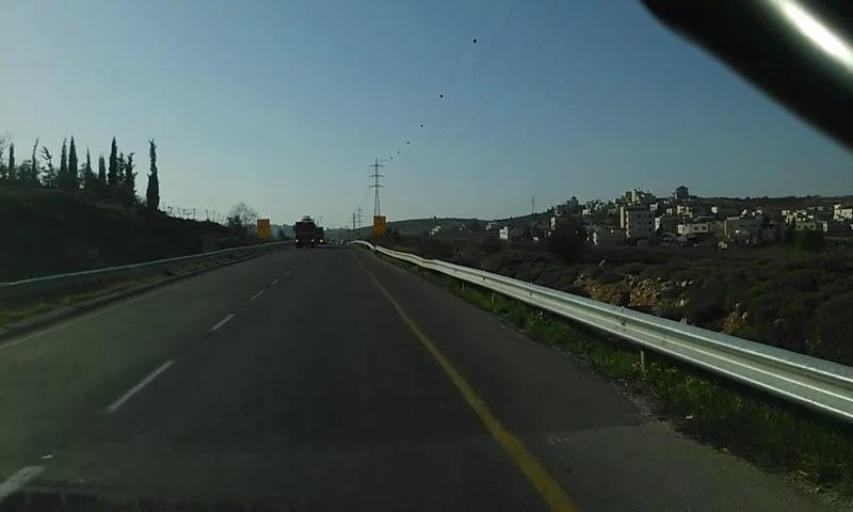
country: PS
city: Bayt `Inun
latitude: 31.5597
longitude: 35.1300
